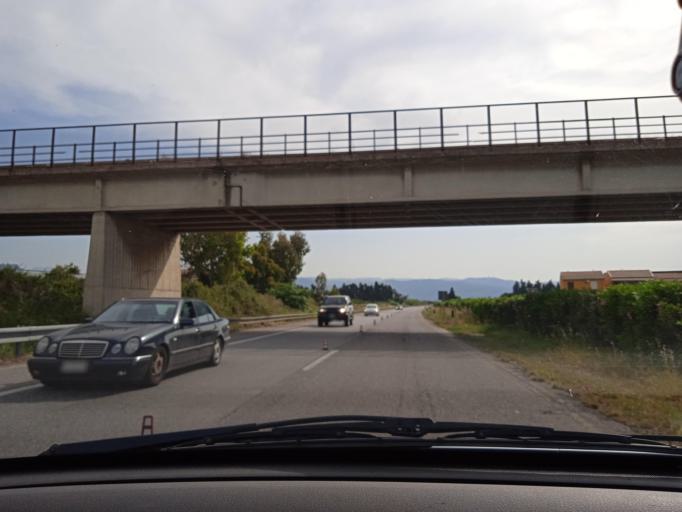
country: IT
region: Sicily
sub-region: Messina
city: Terme
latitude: 38.1452
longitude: 15.1678
